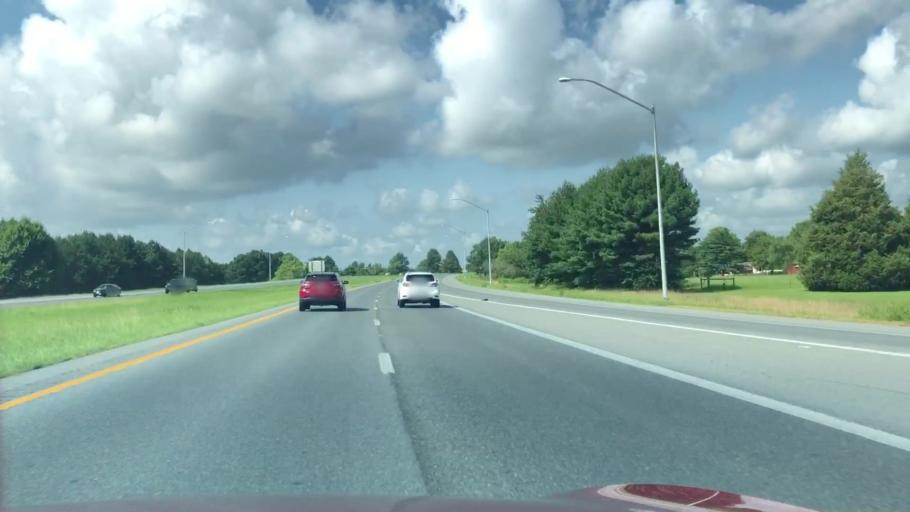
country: US
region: Maryland
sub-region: Wicomico County
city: Fruitland
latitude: 38.3067
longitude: -75.6088
